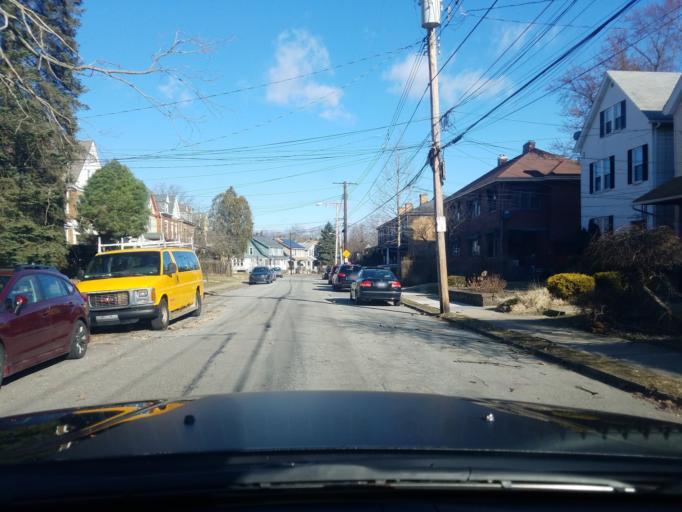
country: US
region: Pennsylvania
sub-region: Allegheny County
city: Wilkinsburg
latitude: 40.4379
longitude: -79.8946
